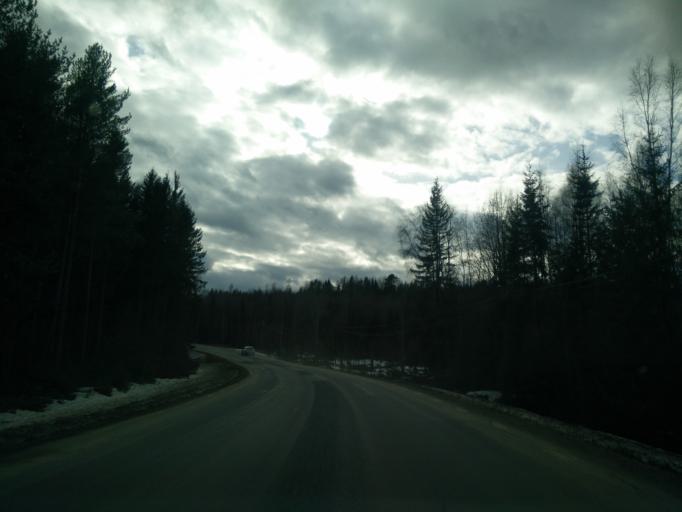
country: SE
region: Vaesternorrland
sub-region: Haernoesands Kommun
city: Haernoesand
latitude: 62.6790
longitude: 17.9196
